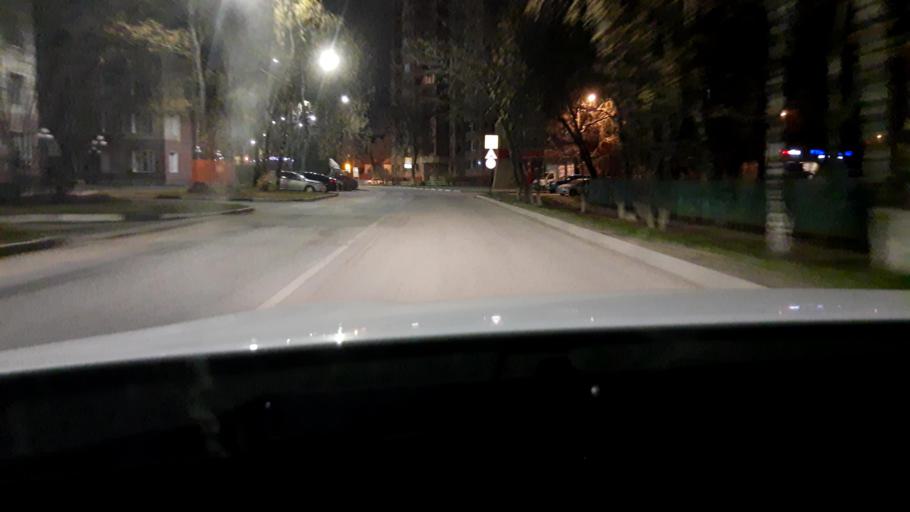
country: RU
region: Moskovskaya
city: Saltykovka
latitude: 55.7480
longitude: 37.9505
